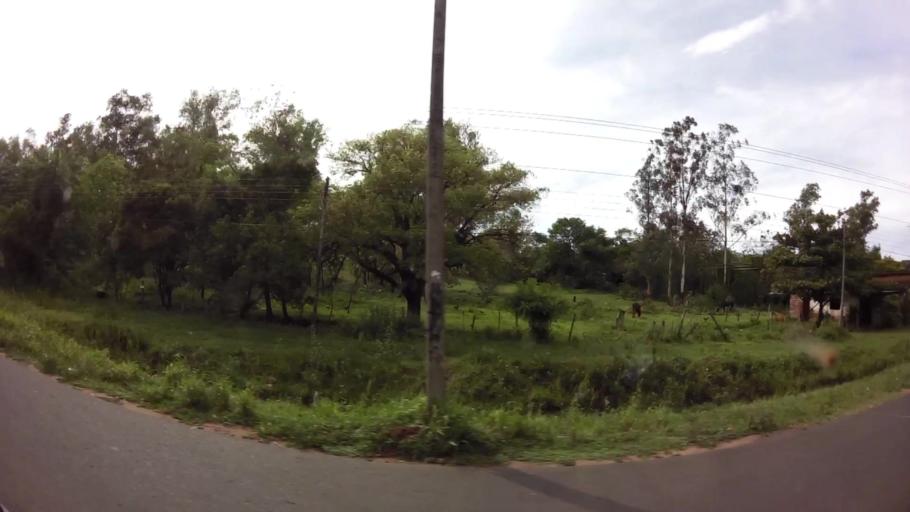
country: PY
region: Central
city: Limpio
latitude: -25.1444
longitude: -57.4580
